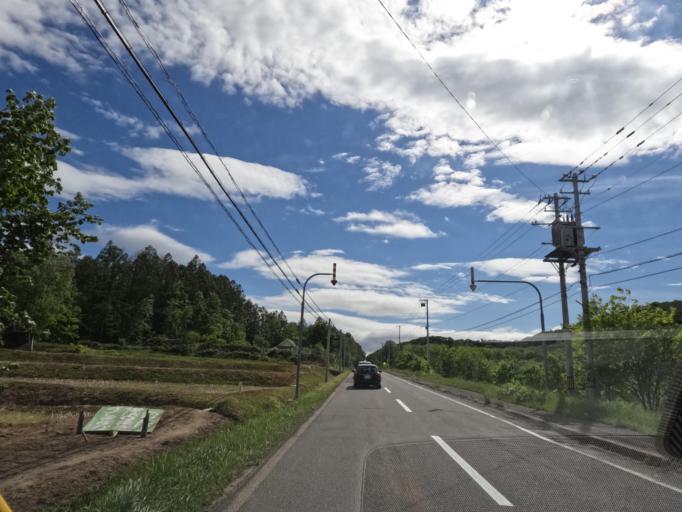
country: JP
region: Hokkaido
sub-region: Asahikawa-shi
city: Asahikawa
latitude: 43.8387
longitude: 142.5425
